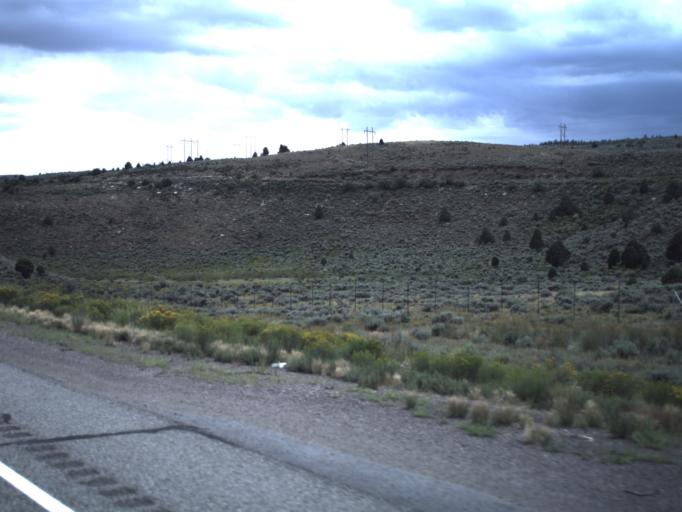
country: US
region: Utah
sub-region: Carbon County
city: Helper
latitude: 39.8278
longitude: -110.9566
